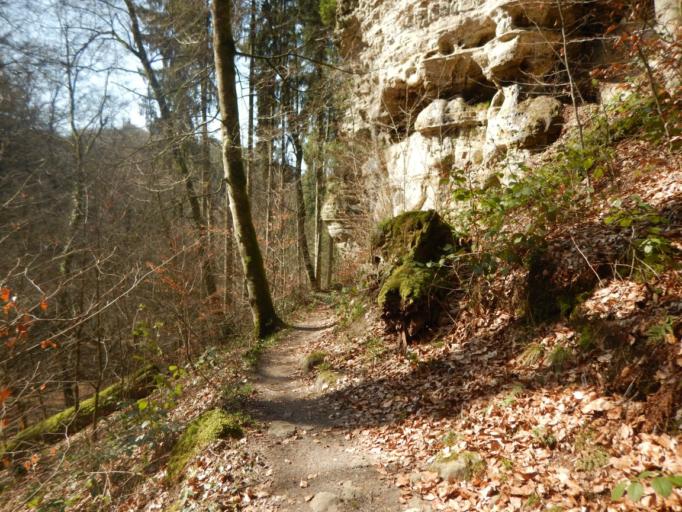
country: LU
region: Grevenmacher
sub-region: Canton d'Echternach
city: Consdorf
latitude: 49.7735
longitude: 6.3600
